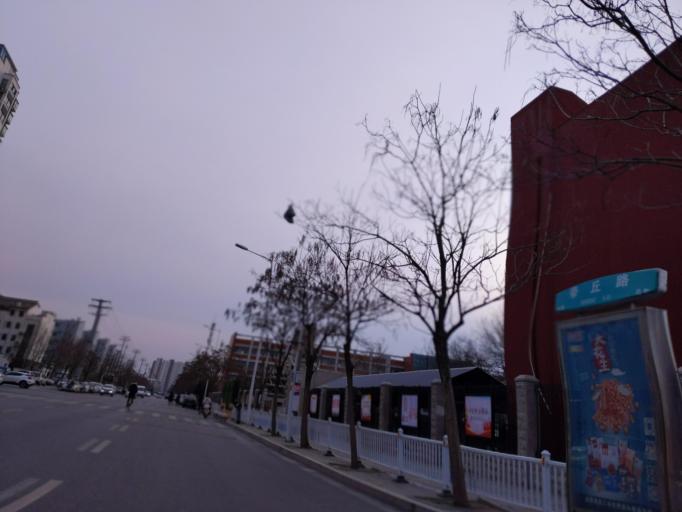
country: CN
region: Henan Sheng
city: Zhongyuanlu
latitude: 35.7605
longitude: 115.0411
